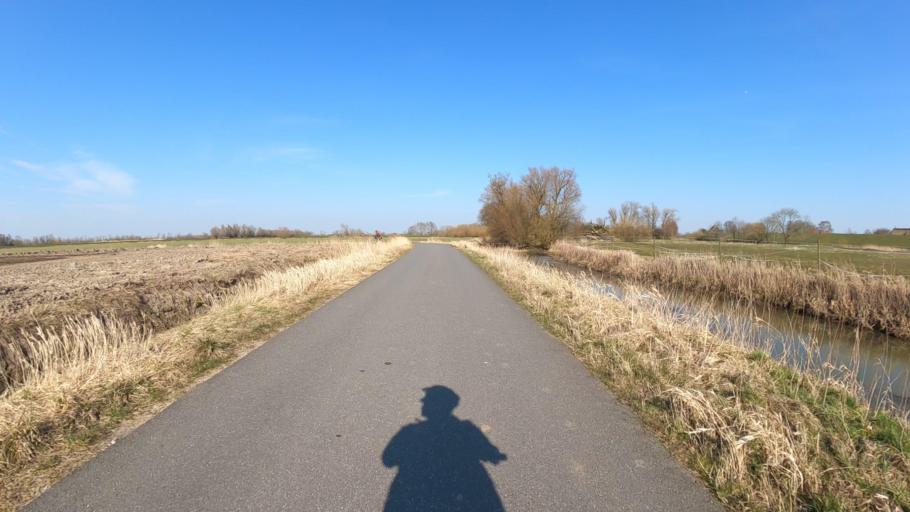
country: DE
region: Schleswig-Holstein
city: Seestermuhe
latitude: 53.7115
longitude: 9.5506
